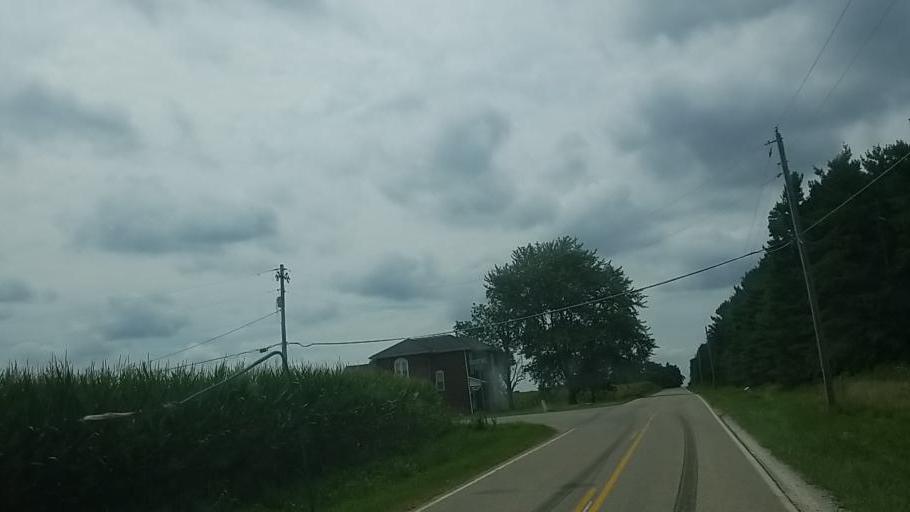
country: US
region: Ohio
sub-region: Fairfield County
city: Lithopolis
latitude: 39.7526
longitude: -82.8559
